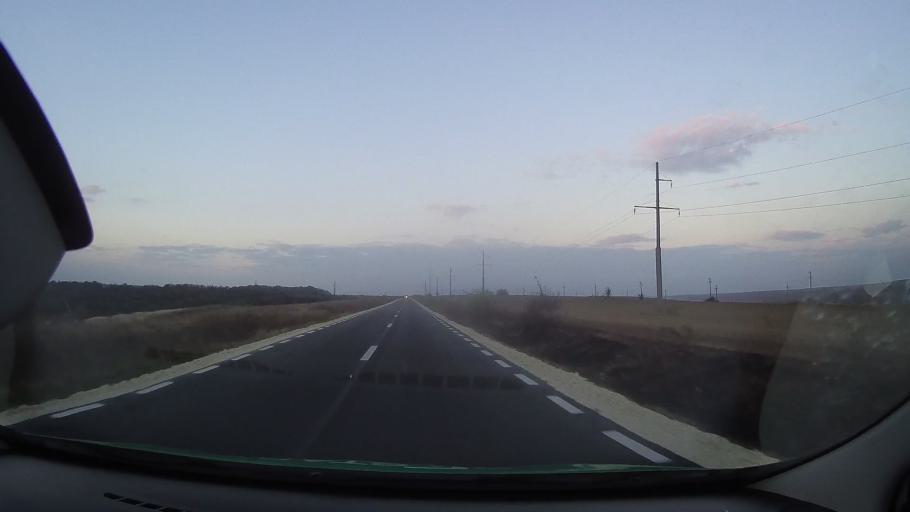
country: RO
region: Constanta
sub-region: Comuna Baneasa
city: Baneasa
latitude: 44.0858
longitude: 27.6881
